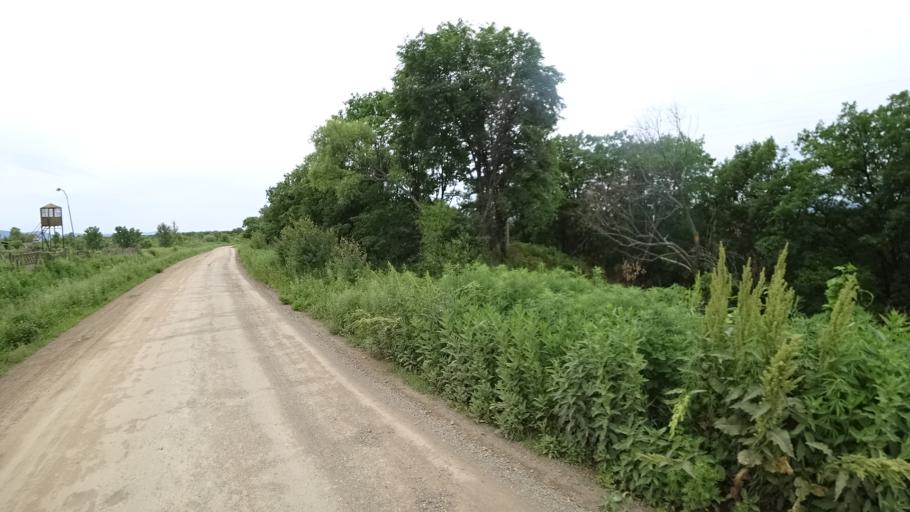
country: RU
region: Primorskiy
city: Arsen'yev
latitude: 44.1999
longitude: 133.3102
